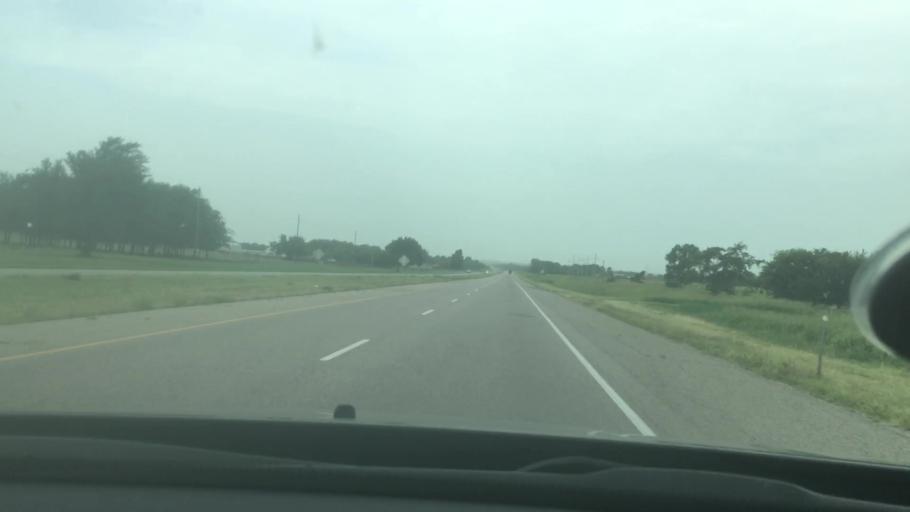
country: US
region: Oklahoma
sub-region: Pontotoc County
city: Ada
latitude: 34.6836
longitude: -96.7643
